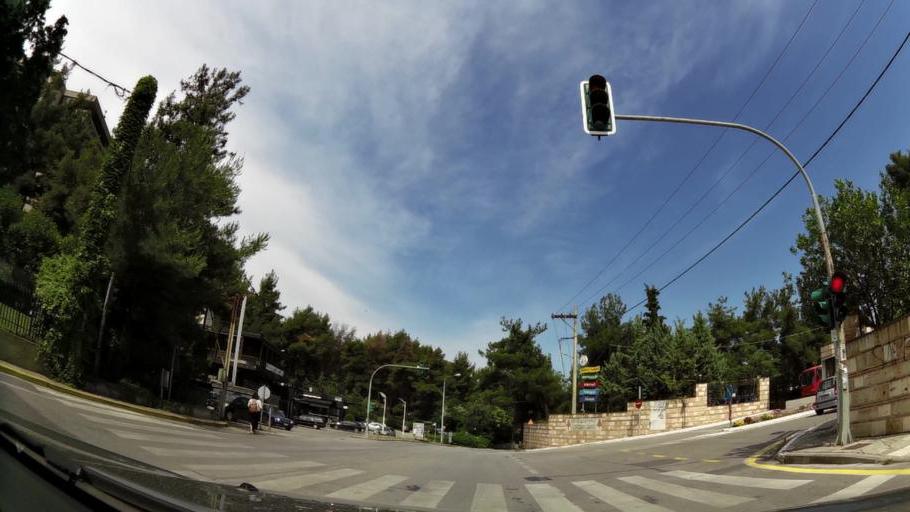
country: GR
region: Central Macedonia
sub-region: Nomos Thessalonikis
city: Pylaia
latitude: 40.5942
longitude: 23.0078
